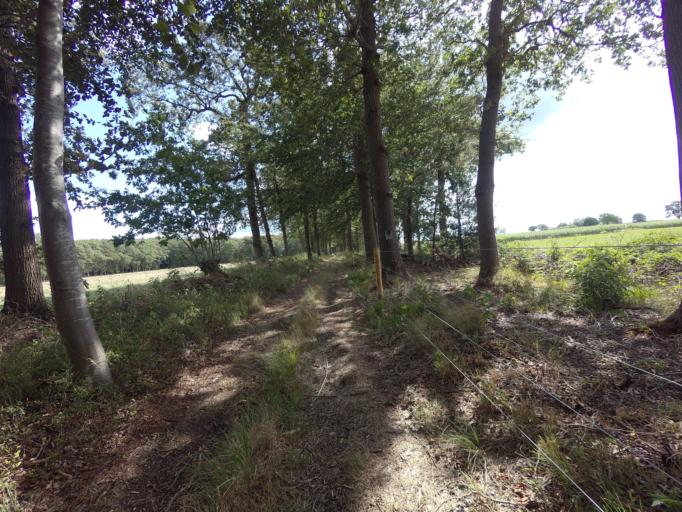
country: NL
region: Friesland
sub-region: Gemeente Weststellingwerf
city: Noordwolde
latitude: 52.9525
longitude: 6.1875
